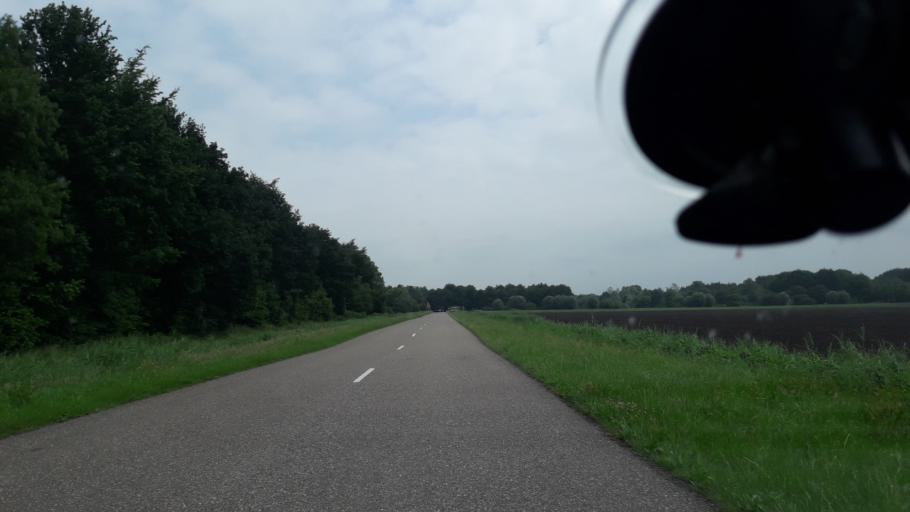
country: NL
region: Flevoland
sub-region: Gemeente Lelystad
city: Lelystad
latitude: 52.4788
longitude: 5.5231
